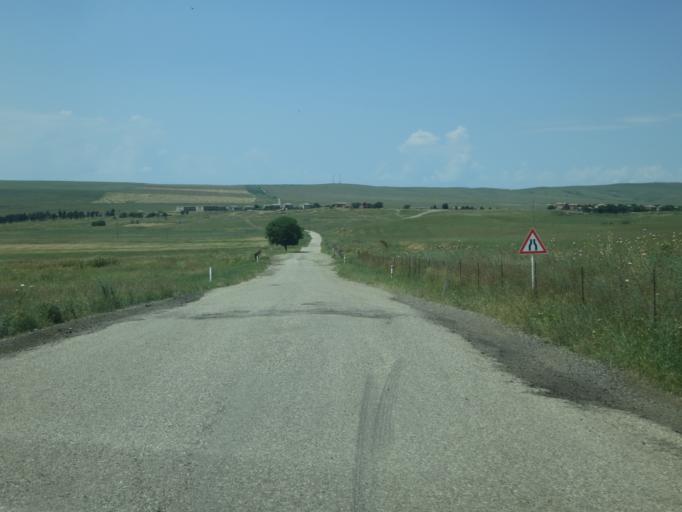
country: GE
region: Kakheti
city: Sagarejo
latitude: 41.5121
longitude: 45.3938
